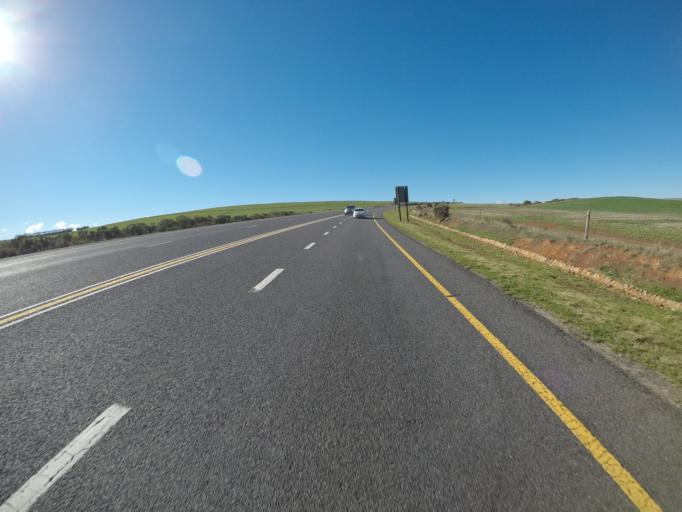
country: ZA
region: Western Cape
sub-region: Overberg District Municipality
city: Caledon
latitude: -34.2306
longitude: 19.2643
